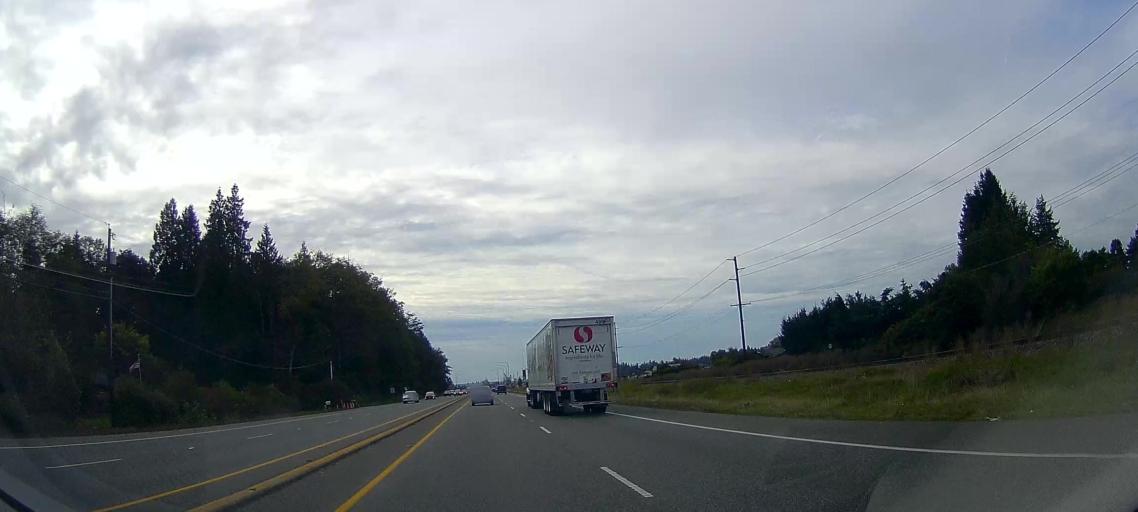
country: US
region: Washington
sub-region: Skagit County
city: Burlington
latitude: 48.4672
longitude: -122.3500
